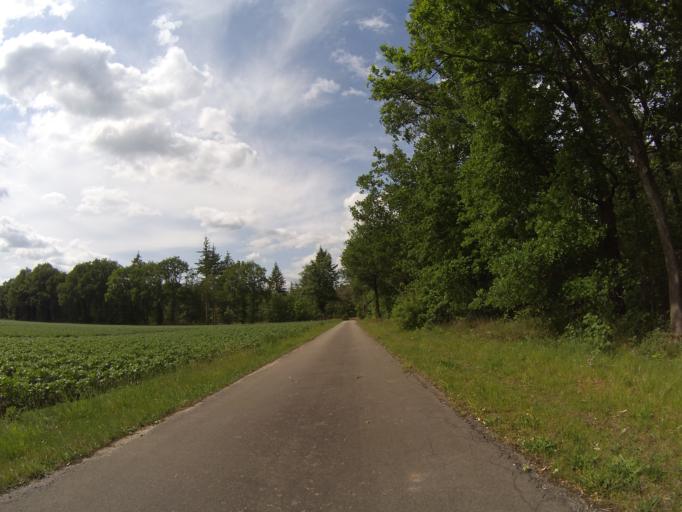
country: NL
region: Drenthe
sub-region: Gemeente Coevorden
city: Sleen
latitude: 52.8005
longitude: 6.8012
